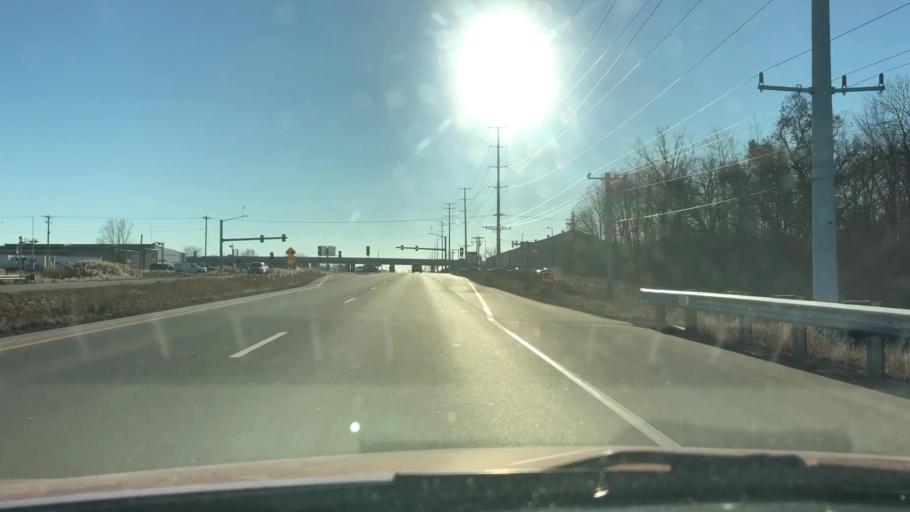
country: US
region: Wisconsin
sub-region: Brown County
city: Ashwaubenon
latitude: 44.4816
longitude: -88.0571
